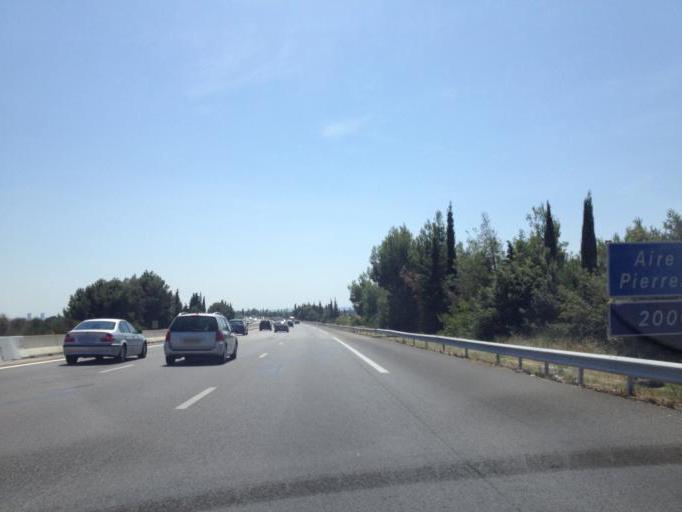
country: FR
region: Rhone-Alpes
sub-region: Departement de la Drome
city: Donzere
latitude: 44.4236
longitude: 4.7358
